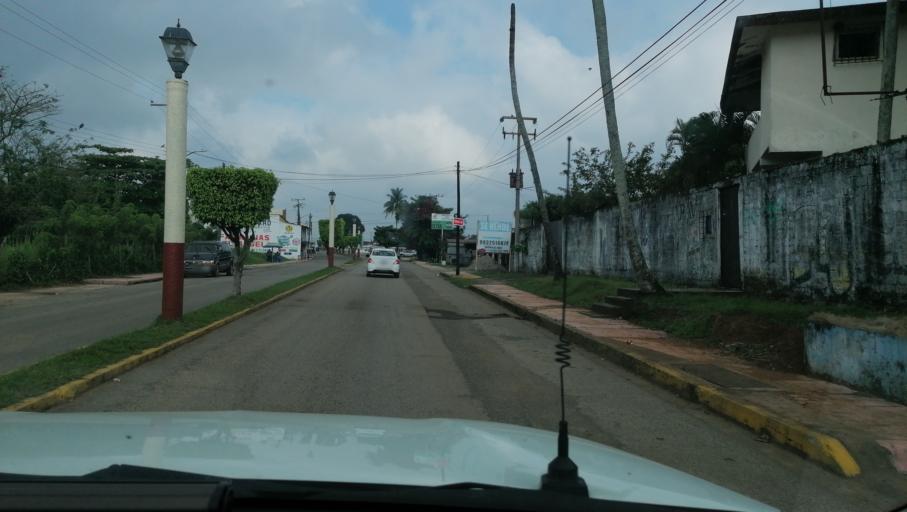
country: MX
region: Chiapas
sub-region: Juarez
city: El Triunfo 1ra. Seccion (Cardona)
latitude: 17.6031
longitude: -93.1858
